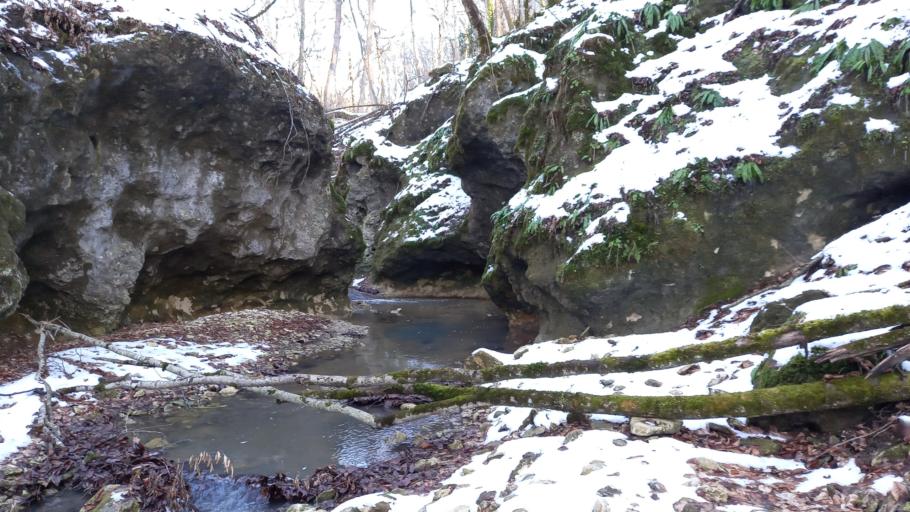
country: RU
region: Adygeya
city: Kamennomostskiy
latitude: 44.2803
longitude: 40.3477
